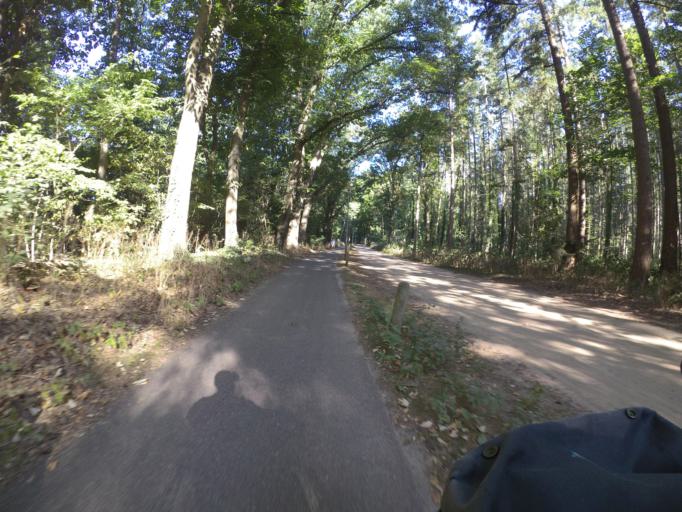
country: NL
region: Gelderland
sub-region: Gemeente Lochem
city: Lochem
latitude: 52.1482
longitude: 6.4128
